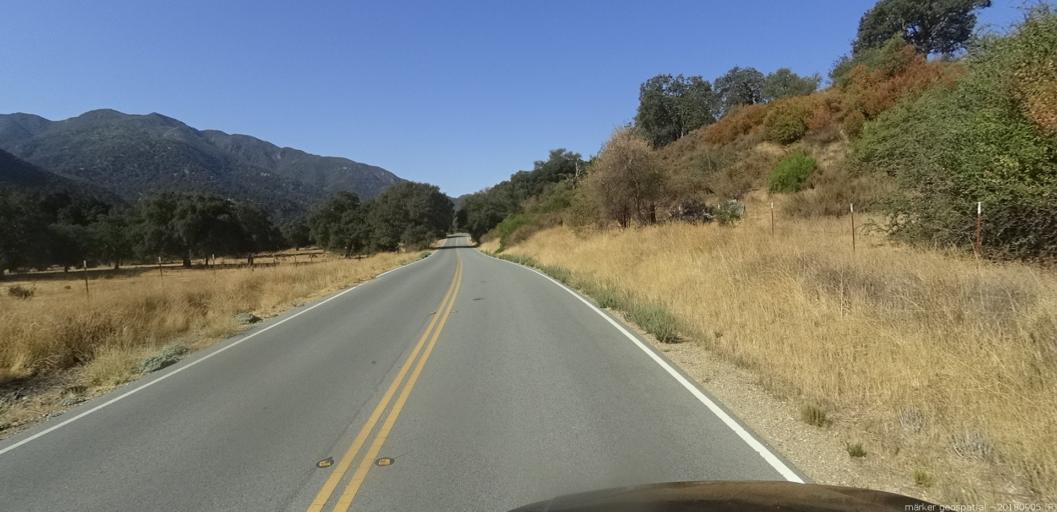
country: US
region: California
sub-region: Monterey County
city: Greenfield
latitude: 36.2378
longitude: -121.4480
